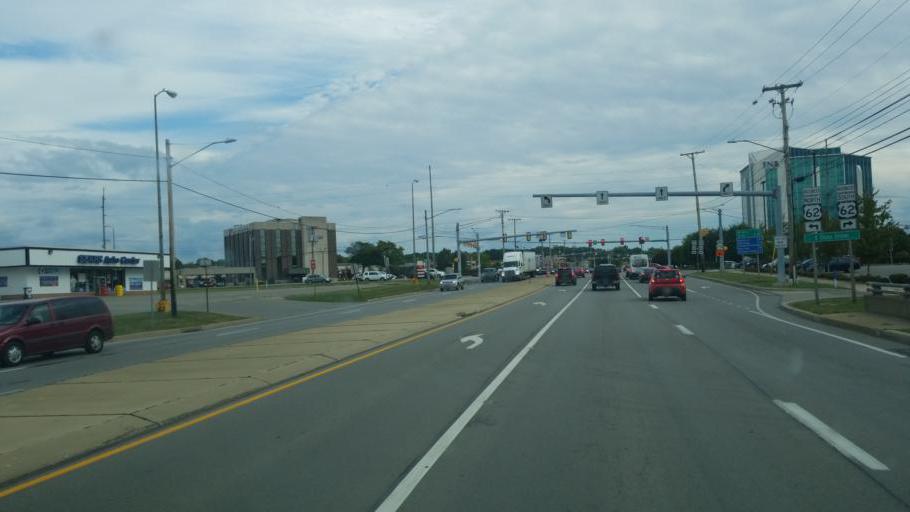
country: US
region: Pennsylvania
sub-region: Mercer County
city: Hermitage
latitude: 41.2345
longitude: -80.4498
